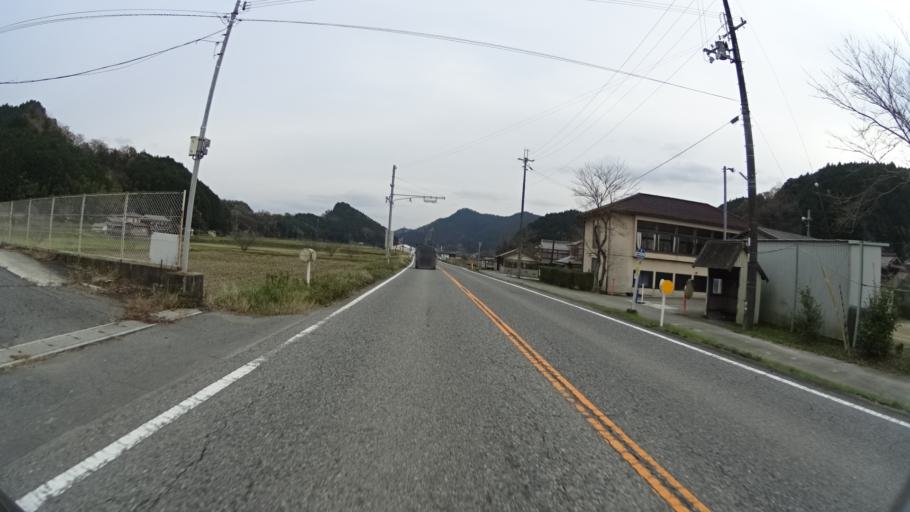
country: JP
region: Hyogo
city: Sasayama
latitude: 35.1047
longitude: 135.1274
